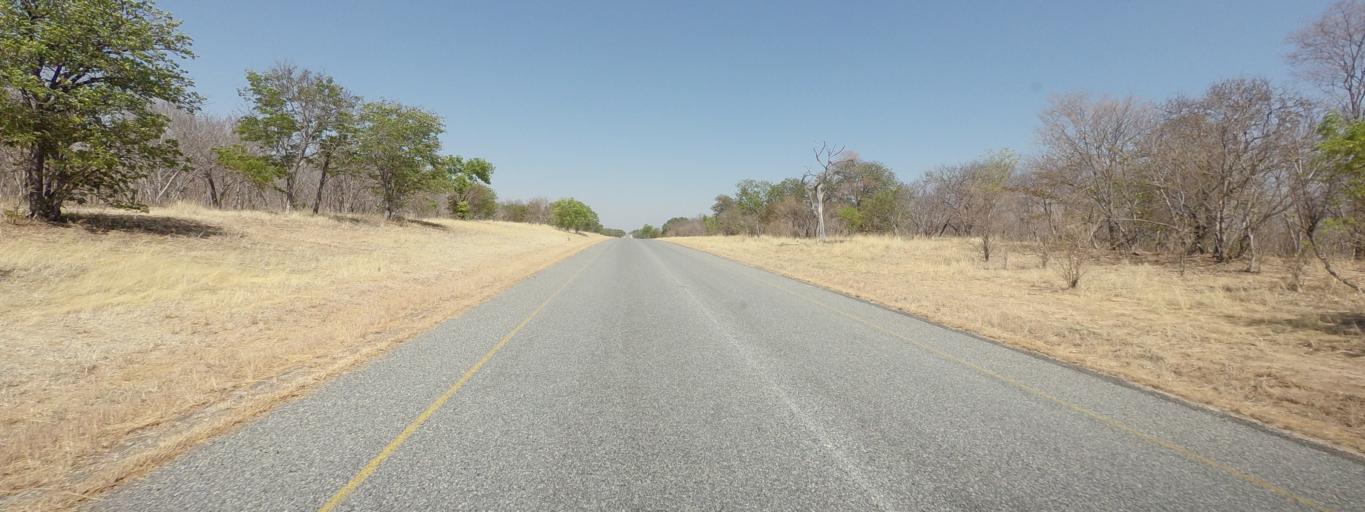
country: BW
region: North West
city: Kasane
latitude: -17.9217
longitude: 25.0259
